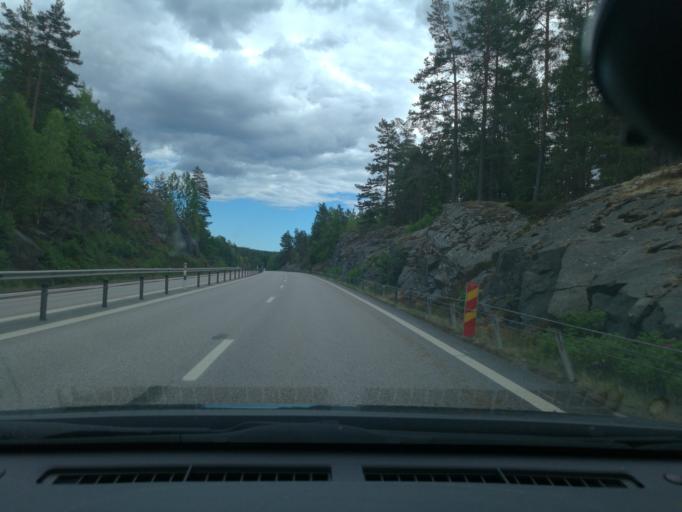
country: SE
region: Kalmar
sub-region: Vasterviks Kommun
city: Forserum
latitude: 58.0284
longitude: 16.5157
